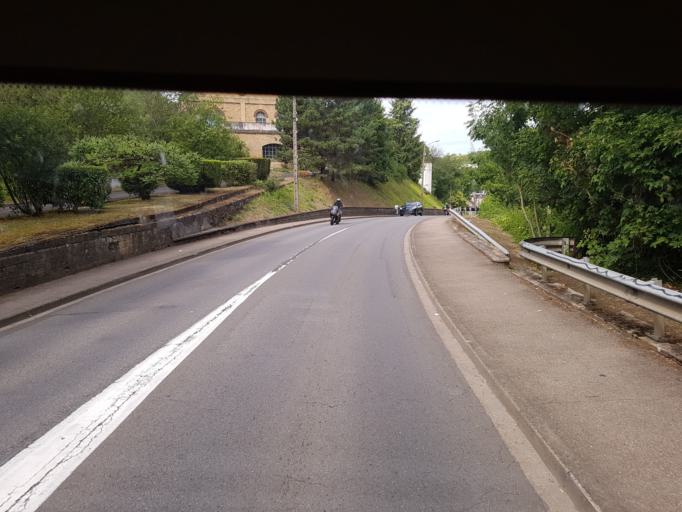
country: FR
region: Lorraine
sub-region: Departement de Meurthe-et-Moselle
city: Homecourt
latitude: 49.2247
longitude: 5.9994
